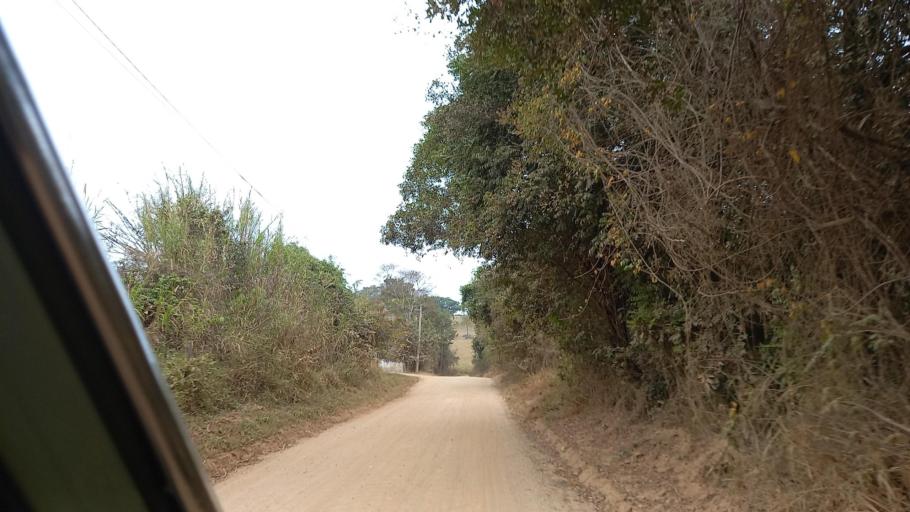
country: BR
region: Sao Paulo
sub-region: Moji-Guacu
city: Mogi-Gaucu
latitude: -22.3001
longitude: -46.8331
